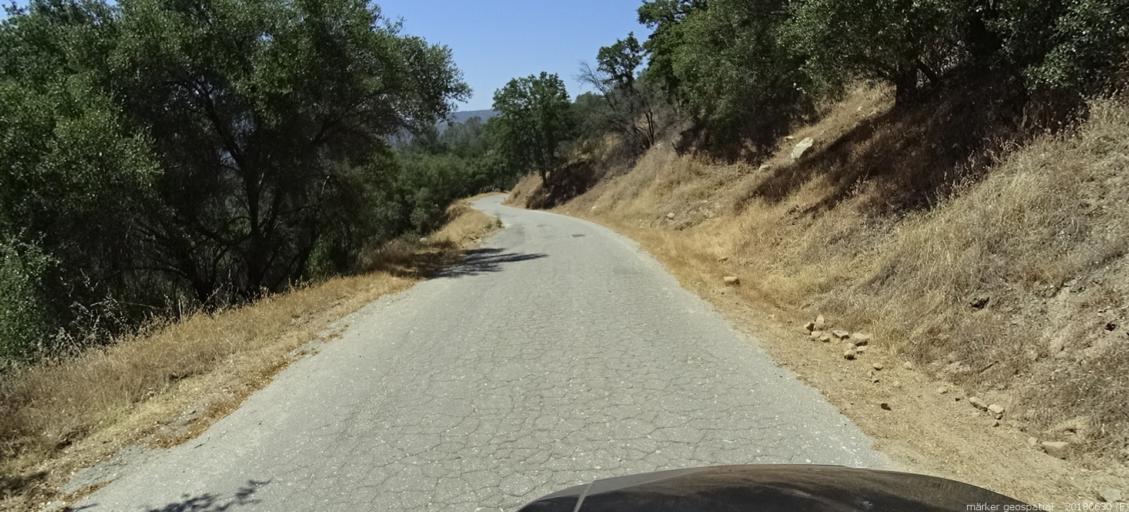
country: US
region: California
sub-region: Fresno County
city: Auberry
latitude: 37.1428
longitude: -119.4886
